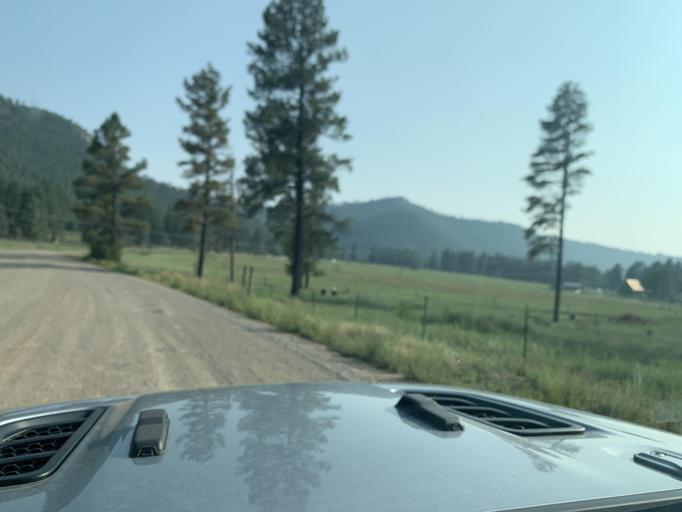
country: US
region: Colorado
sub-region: Archuleta County
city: Pagosa Springs
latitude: 37.2220
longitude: -107.2103
